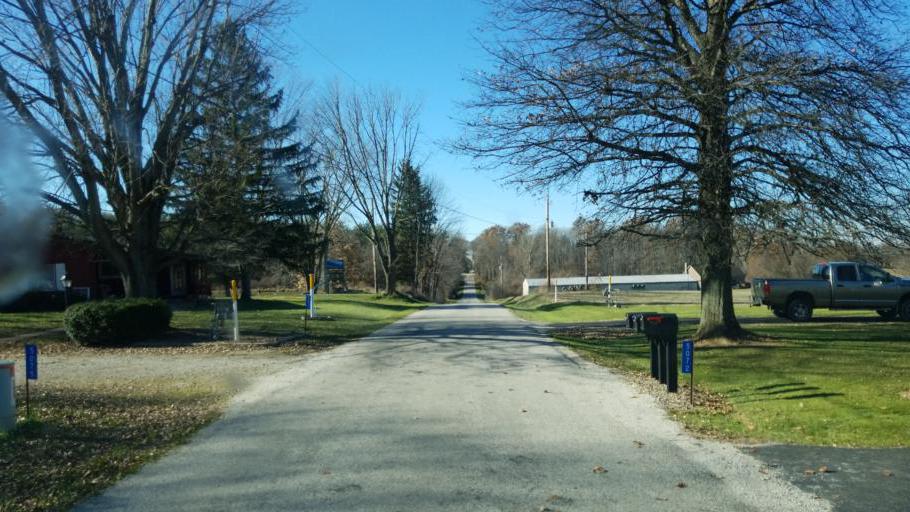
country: US
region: Ohio
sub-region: Huron County
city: Plymouth
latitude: 40.9522
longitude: -82.6977
